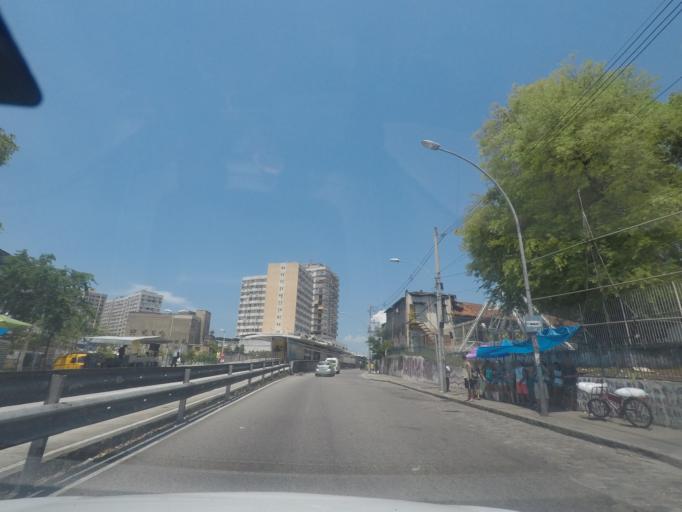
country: BR
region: Rio de Janeiro
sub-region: Duque De Caxias
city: Duque de Caxias
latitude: -22.8423
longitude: -43.2776
